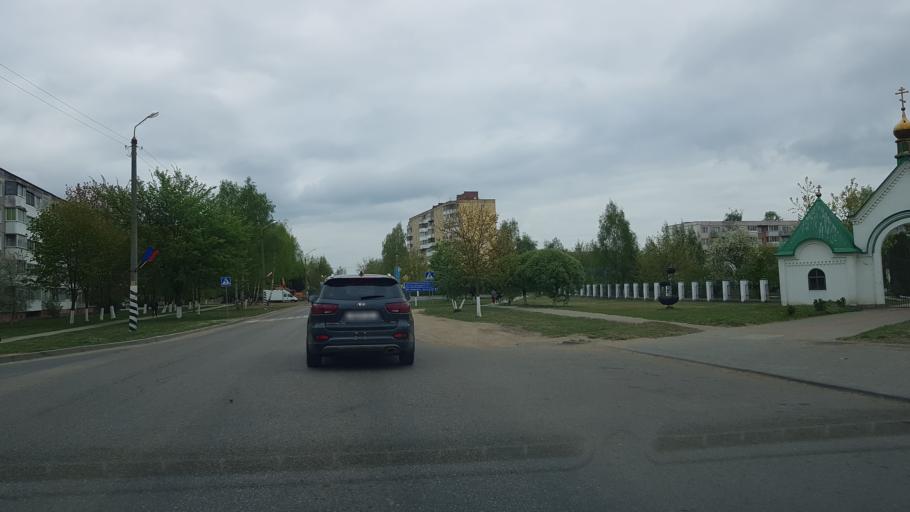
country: BY
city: Fanipol
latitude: 53.7388
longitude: 27.3142
